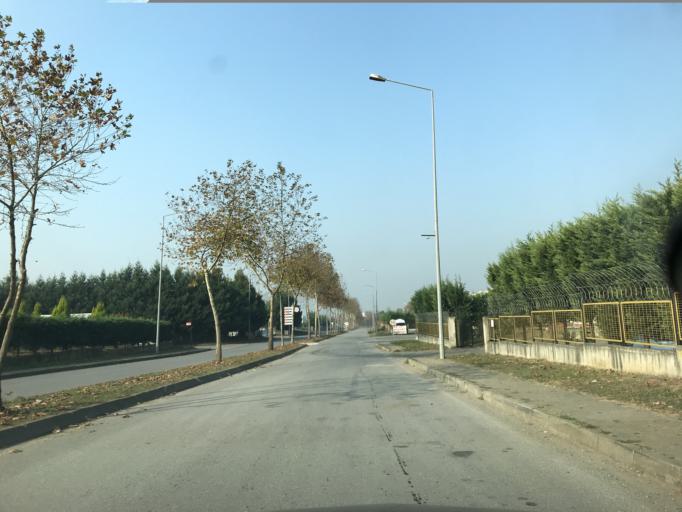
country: TR
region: Duzce
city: Duzce
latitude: 40.7851
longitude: 31.1467
